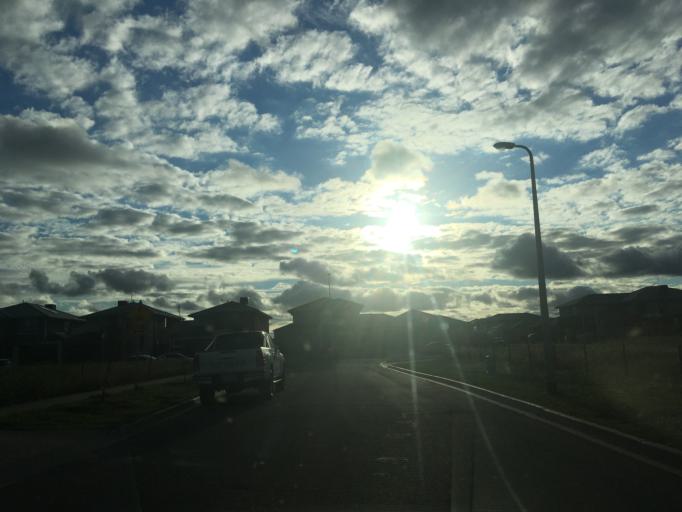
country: AU
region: Victoria
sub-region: Wyndham
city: Hoppers Crossing
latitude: -37.8896
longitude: 144.7140
